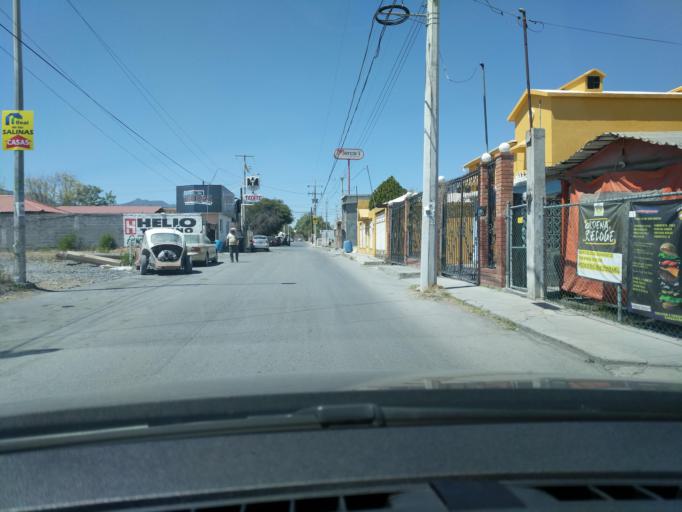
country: MX
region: Nuevo Leon
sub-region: Salinas Victoria
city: Las Torres
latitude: 25.9648
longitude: -100.2951
